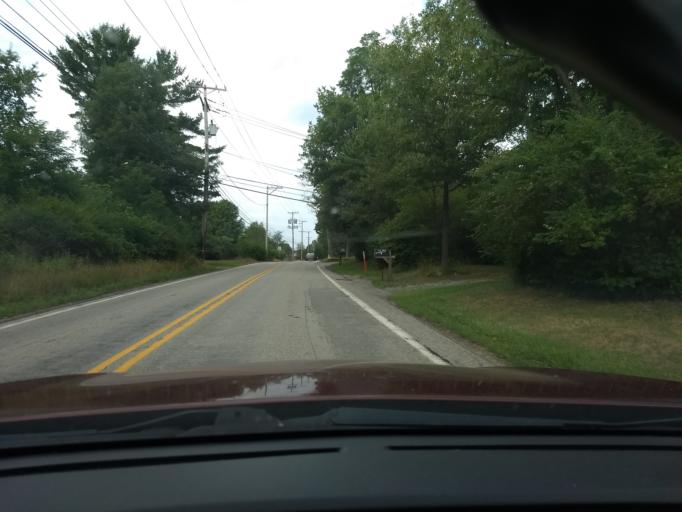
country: US
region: Pennsylvania
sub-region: Allegheny County
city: Curtisville
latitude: 40.6579
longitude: -79.8840
